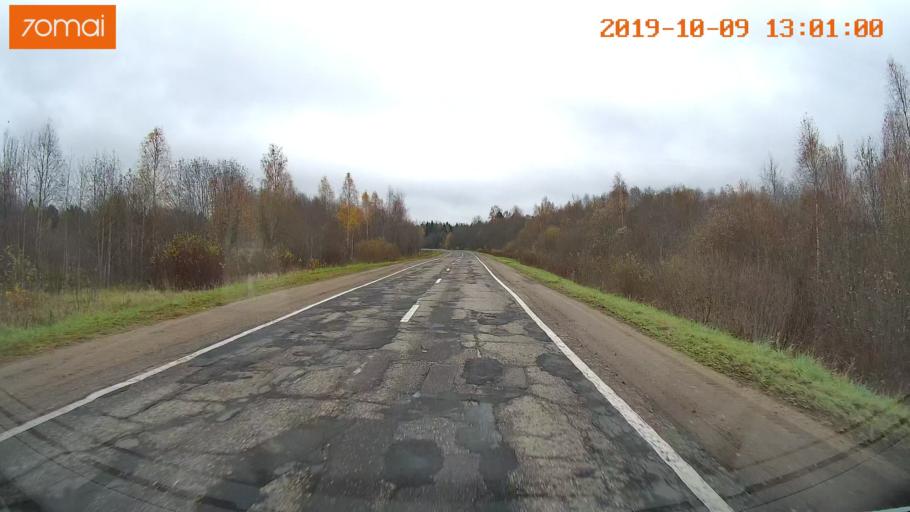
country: RU
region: Jaroslavl
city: Prechistoye
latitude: 58.3720
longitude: 40.4838
